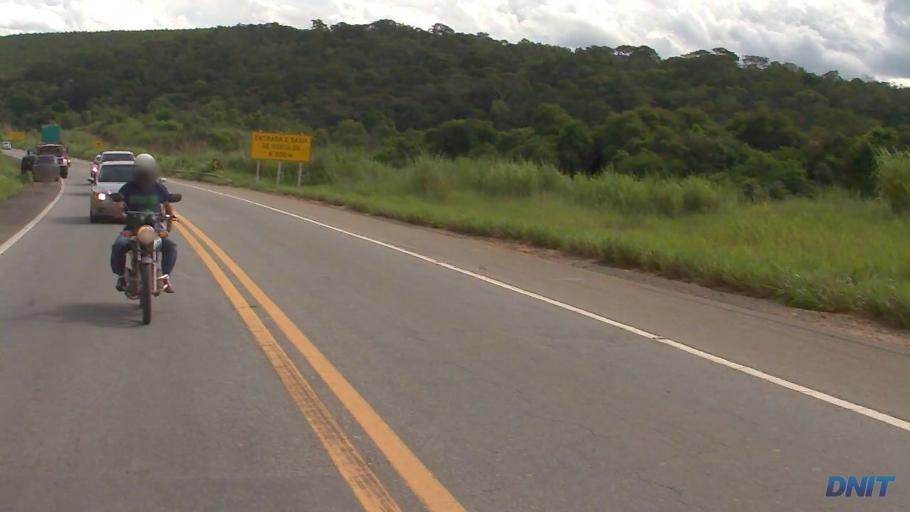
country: BR
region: Minas Gerais
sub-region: Ipaba
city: Ipaba
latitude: -19.3536
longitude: -42.4347
